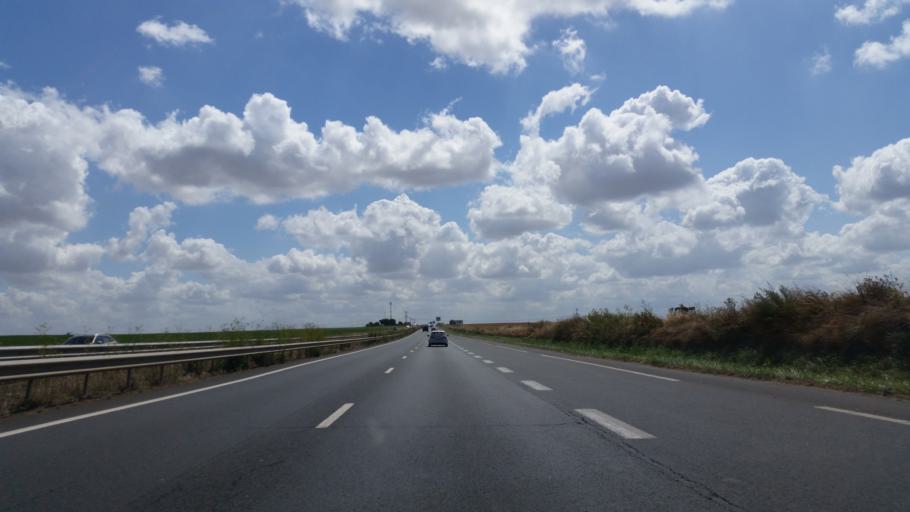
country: FR
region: Lower Normandy
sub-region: Departement du Calvados
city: Bourguebus
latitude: 49.1216
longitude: -0.3253
